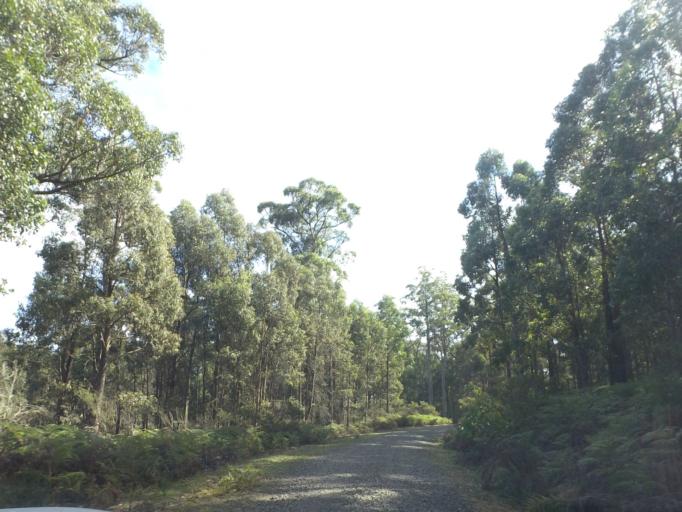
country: AU
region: Victoria
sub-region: Moorabool
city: Bacchus Marsh
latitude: -37.4339
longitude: 144.2431
